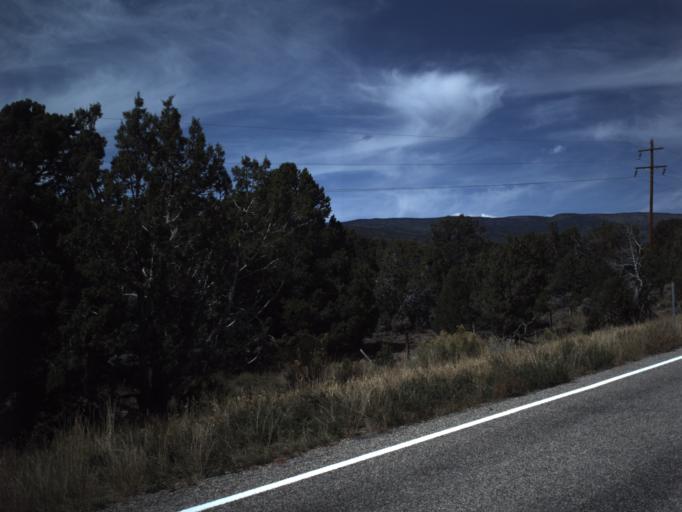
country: US
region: Utah
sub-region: Wayne County
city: Loa
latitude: 37.9501
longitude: -111.4337
